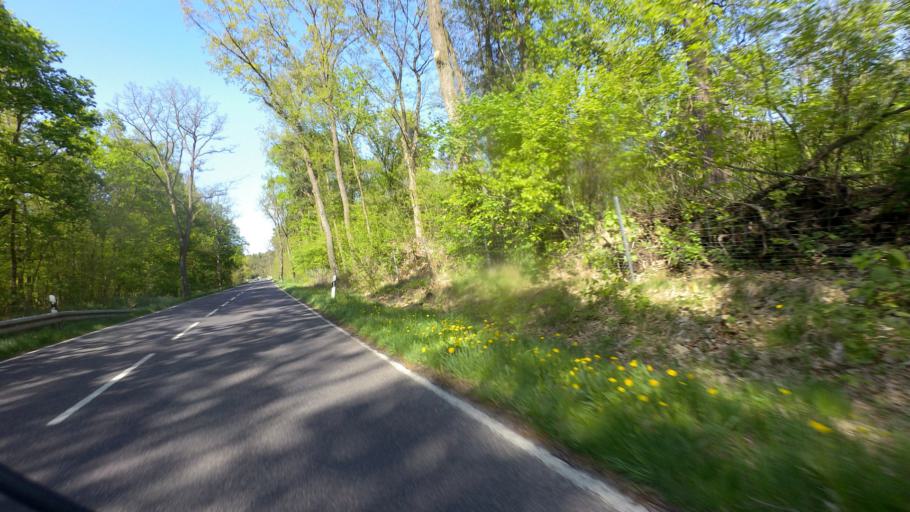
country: DE
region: Brandenburg
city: Halbe
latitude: 52.1126
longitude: 13.7590
